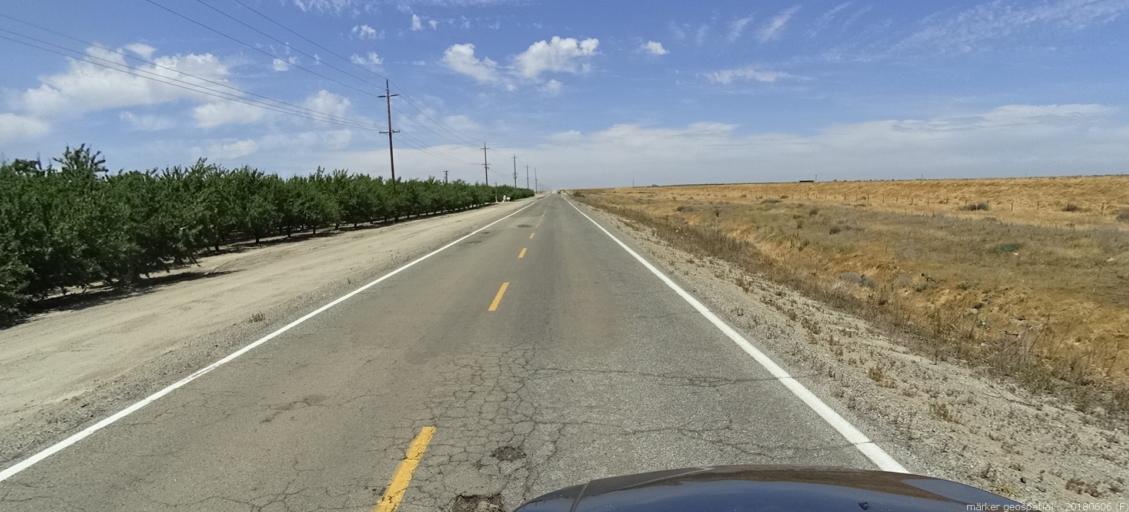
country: US
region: California
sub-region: Fresno County
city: Mendota
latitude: 36.8460
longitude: -120.3168
